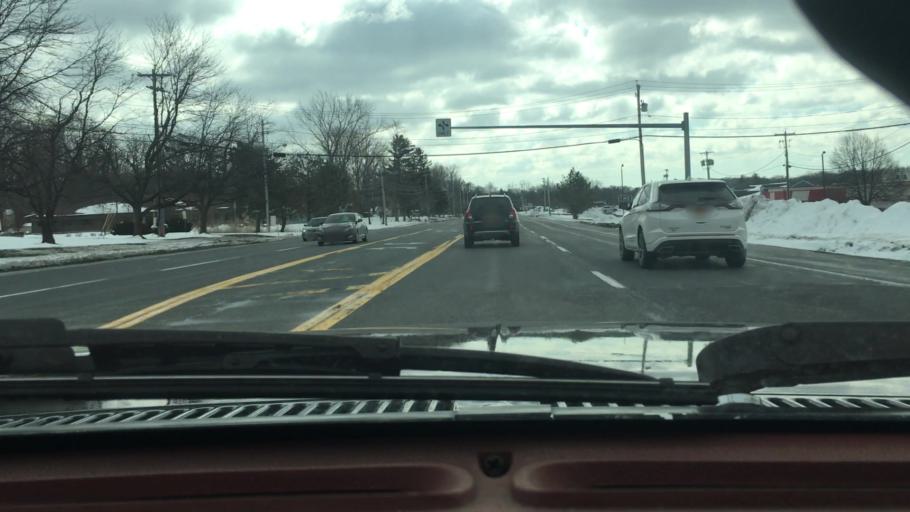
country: US
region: New York
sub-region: Onondaga County
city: Liverpool
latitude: 43.1623
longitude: -76.2338
